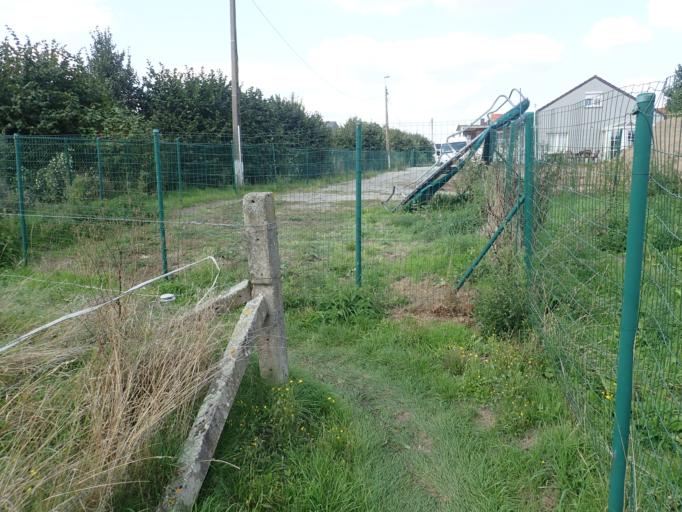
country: BE
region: Flanders
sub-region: Provincie Vlaams-Brabant
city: Opwijk
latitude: 50.9541
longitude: 4.1820
